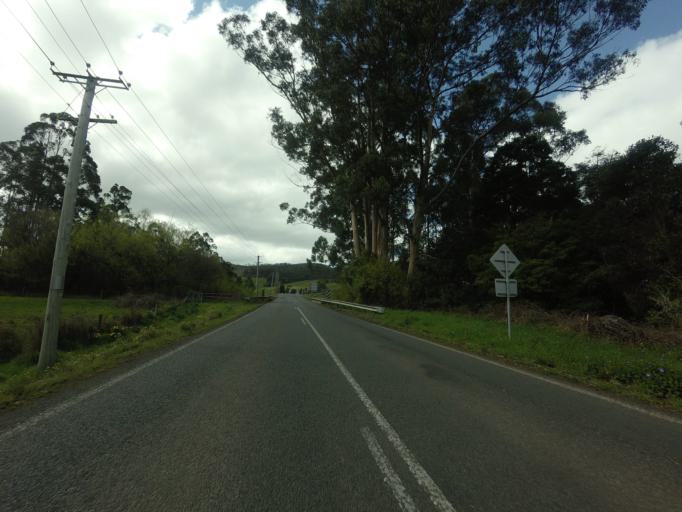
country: AU
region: Tasmania
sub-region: Huon Valley
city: Cygnet
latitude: -43.2979
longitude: 147.0099
